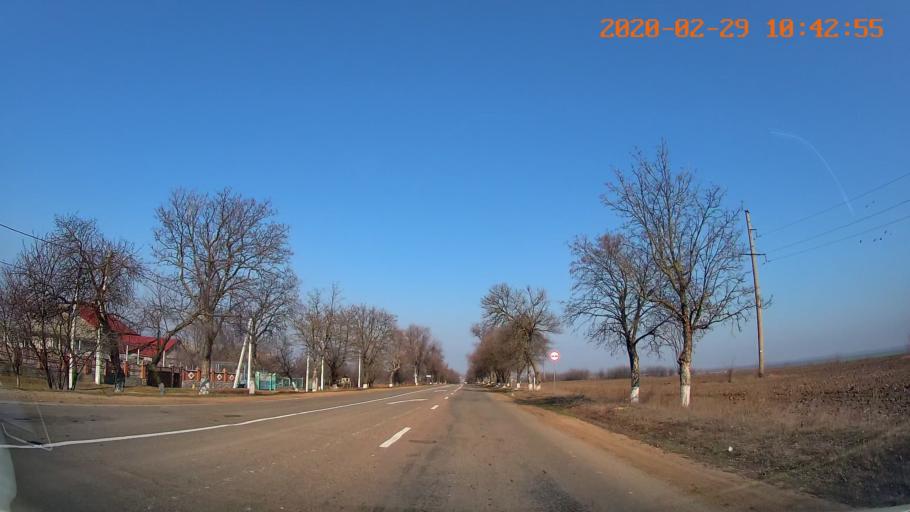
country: MD
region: Telenesti
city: Grigoriopol
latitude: 47.0555
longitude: 29.4059
